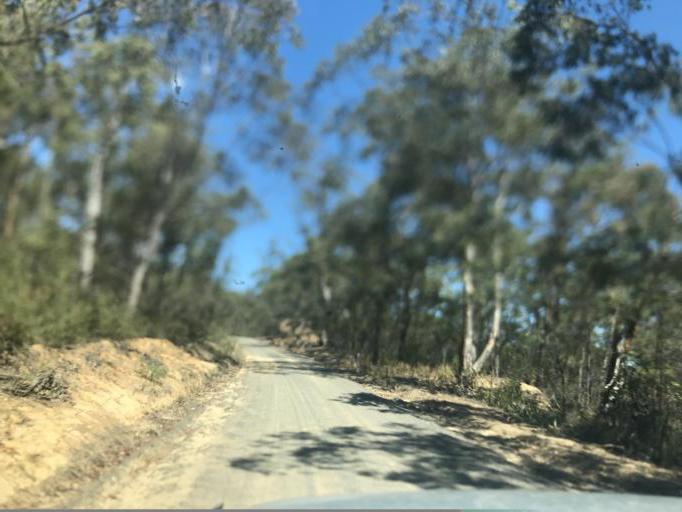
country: AU
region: New South Wales
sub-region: Wyong Shire
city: Little Jilliby
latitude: -33.1441
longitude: 151.0901
